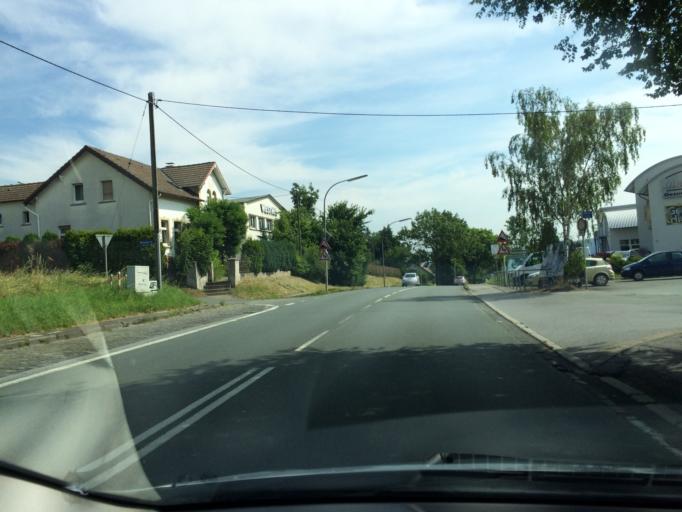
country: DE
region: North Rhine-Westphalia
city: Hemer
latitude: 51.3886
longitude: 7.7467
